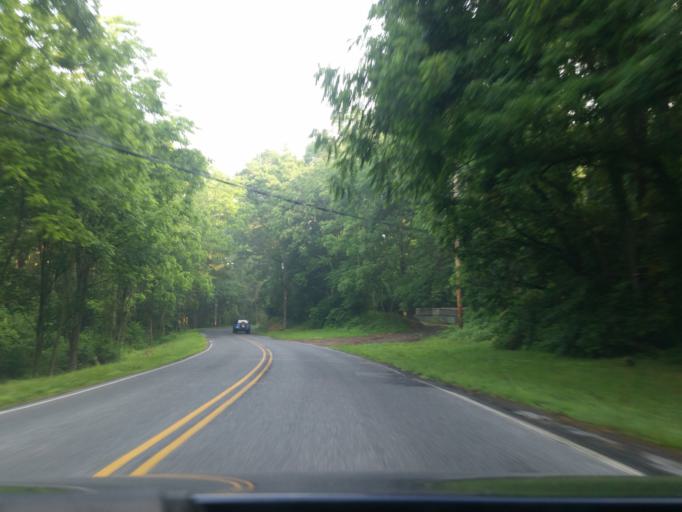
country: US
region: Pennsylvania
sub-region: Lebanon County
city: Annville
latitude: 40.3418
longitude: -76.5008
